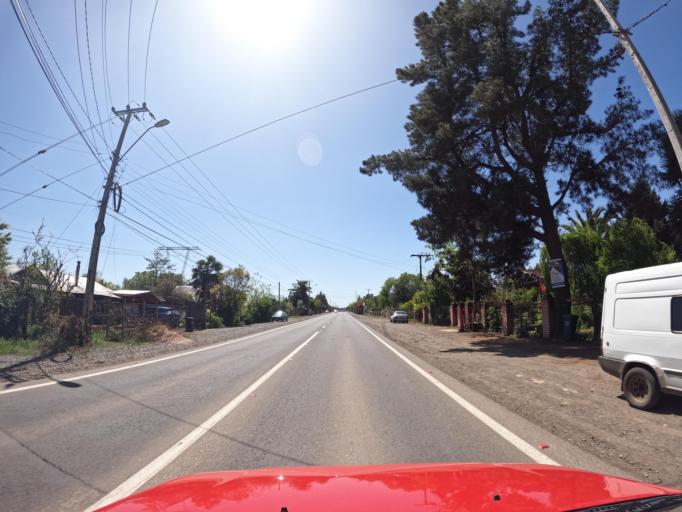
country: CL
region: Maule
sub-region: Provincia de Linares
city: Colbun
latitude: -35.7412
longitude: -71.4222
